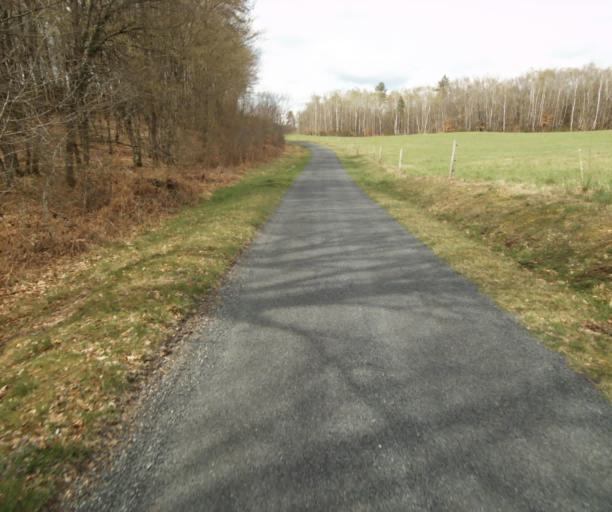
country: FR
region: Limousin
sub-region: Departement de la Correze
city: Argentat
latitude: 45.2205
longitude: 1.9092
